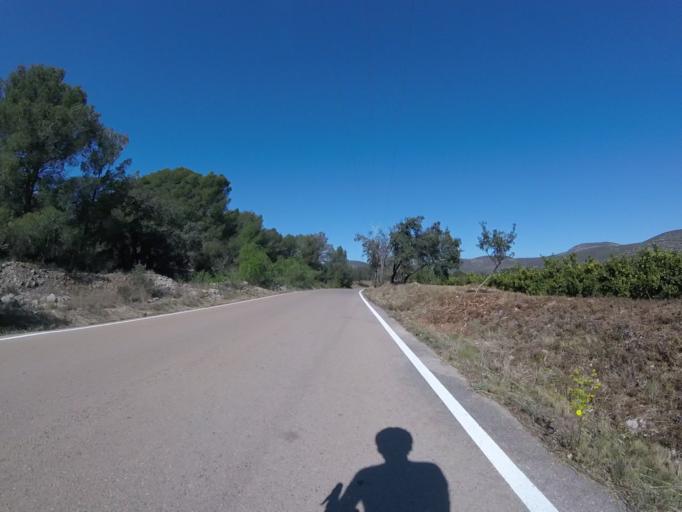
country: ES
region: Valencia
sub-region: Provincia de Castello
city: Santa Magdalena de Pulpis
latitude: 40.3646
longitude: 0.2782
